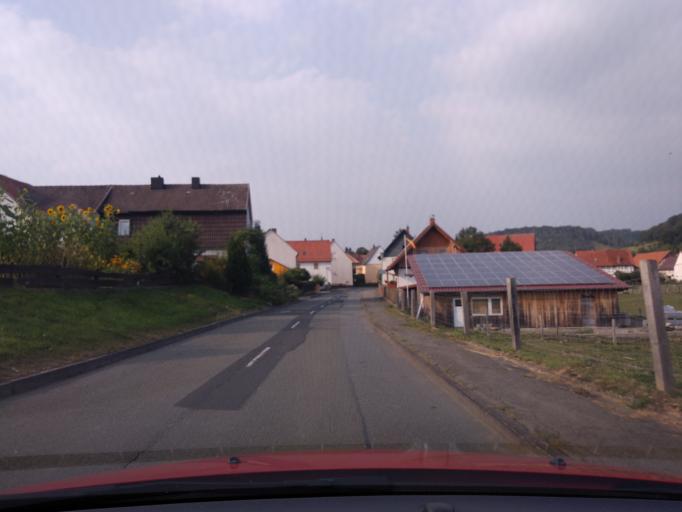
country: DE
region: Hesse
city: Liebenau
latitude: 51.4791
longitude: 9.2969
